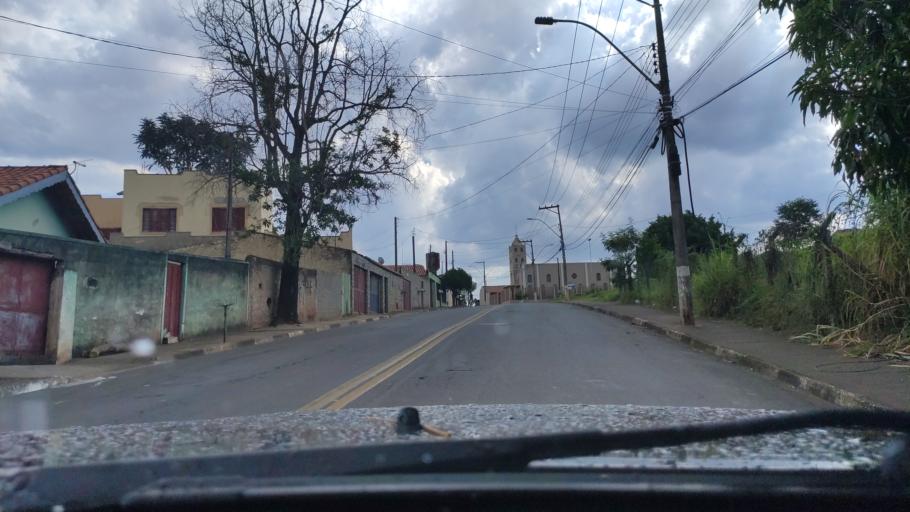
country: BR
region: Sao Paulo
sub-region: Itapira
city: Itapira
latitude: -22.4378
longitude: -46.8080
